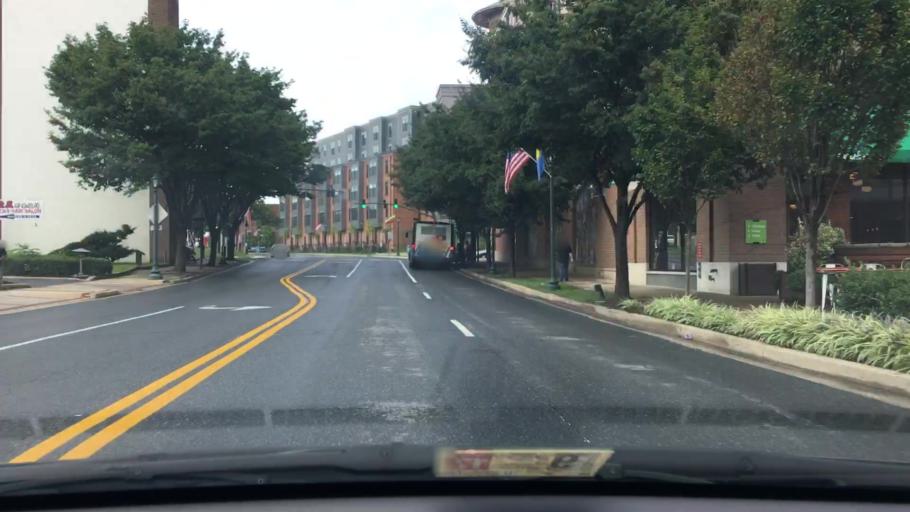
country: US
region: Maryland
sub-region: Montgomery County
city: Rockville
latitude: 39.0860
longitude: -77.1530
